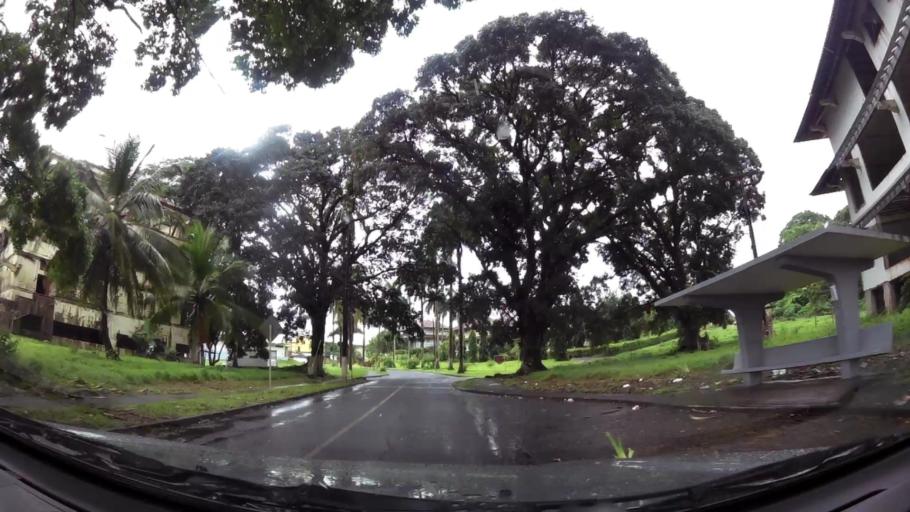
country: PA
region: Colon
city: Las Margaritas
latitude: 9.3137
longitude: -79.8760
